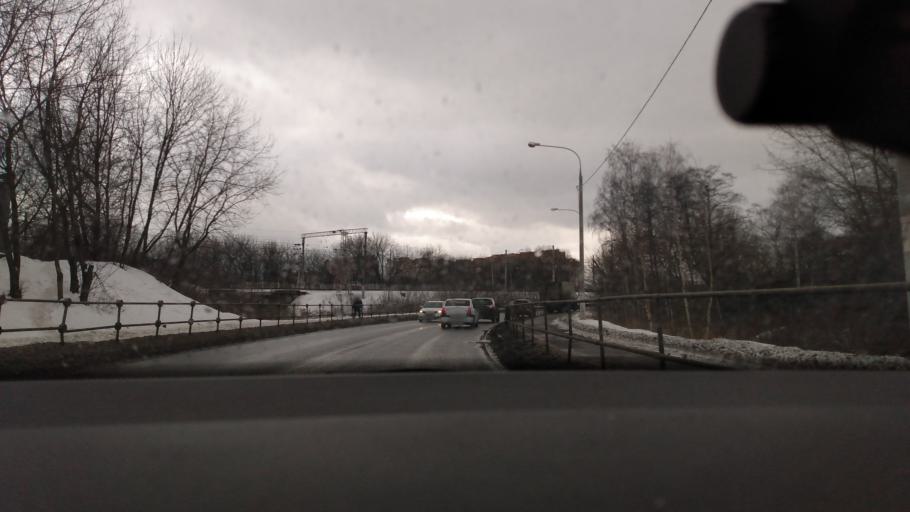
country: RU
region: Moskovskaya
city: Shchelkovo
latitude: 55.9108
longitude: 37.9974
